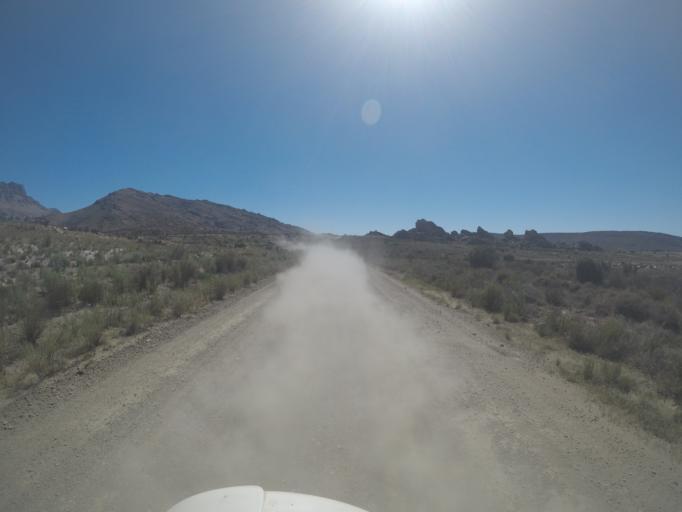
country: ZA
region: Western Cape
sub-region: Cape Winelands District Municipality
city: Ceres
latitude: -32.8586
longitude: 19.4440
